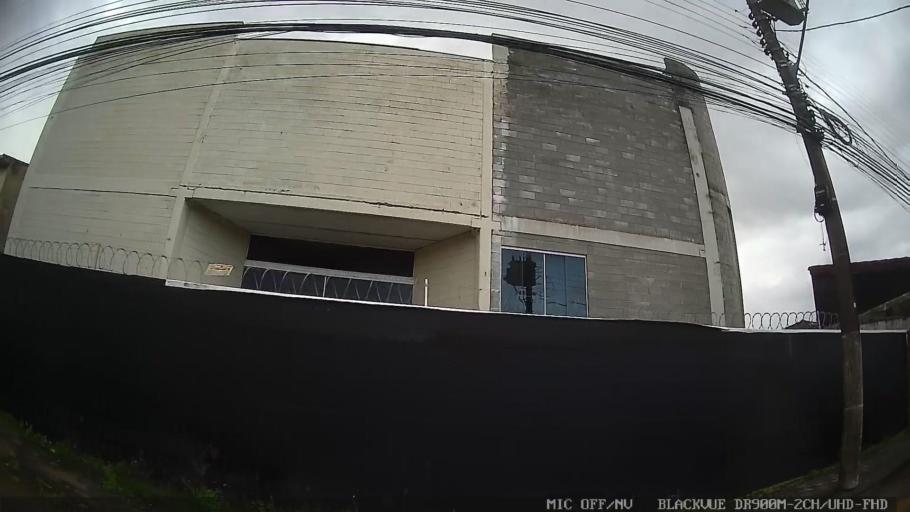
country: BR
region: Sao Paulo
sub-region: Itanhaem
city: Itanhaem
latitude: -24.1815
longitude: -46.7871
